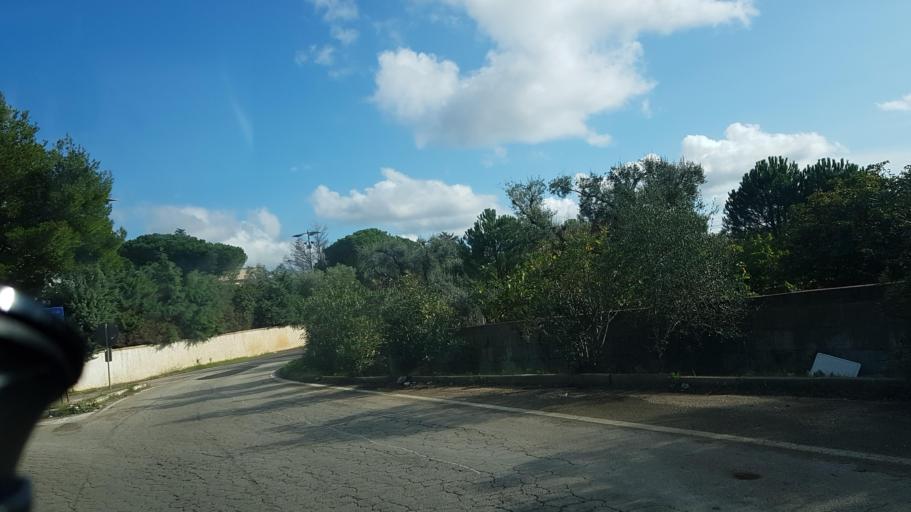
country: IT
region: Apulia
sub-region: Provincia di Brindisi
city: San Michele Salentino
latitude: 40.6462
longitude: 17.6074
